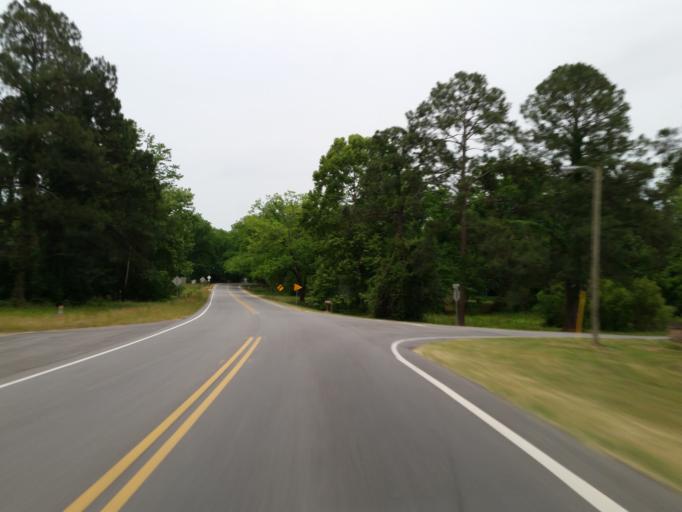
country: US
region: Georgia
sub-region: Crisp County
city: Cordele
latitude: 31.9302
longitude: -83.7775
